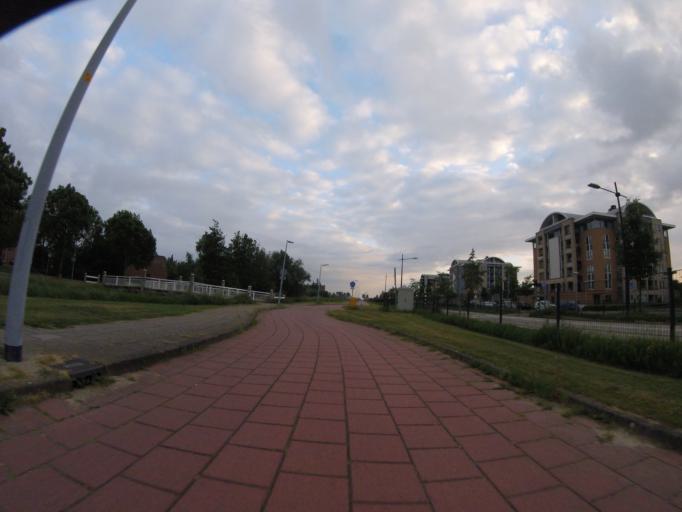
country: NL
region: North Holland
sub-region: Gemeente Haarlemmermeer
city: Hoofddorp
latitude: 52.2982
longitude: 4.6615
